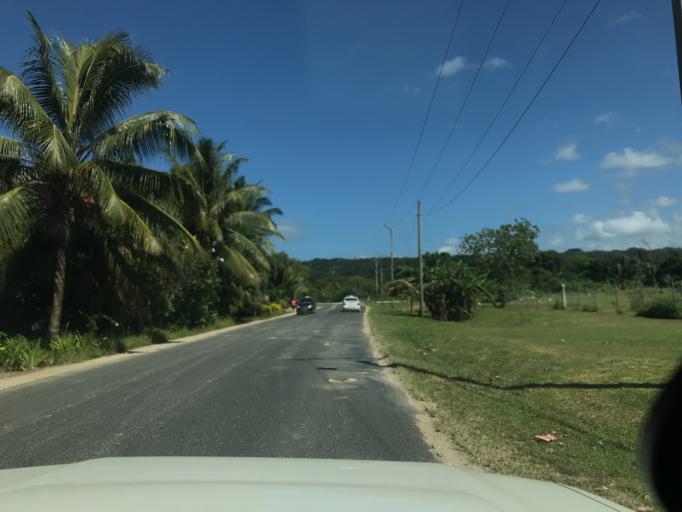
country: VU
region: Sanma
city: Luganville
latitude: -15.5188
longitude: 167.1639
